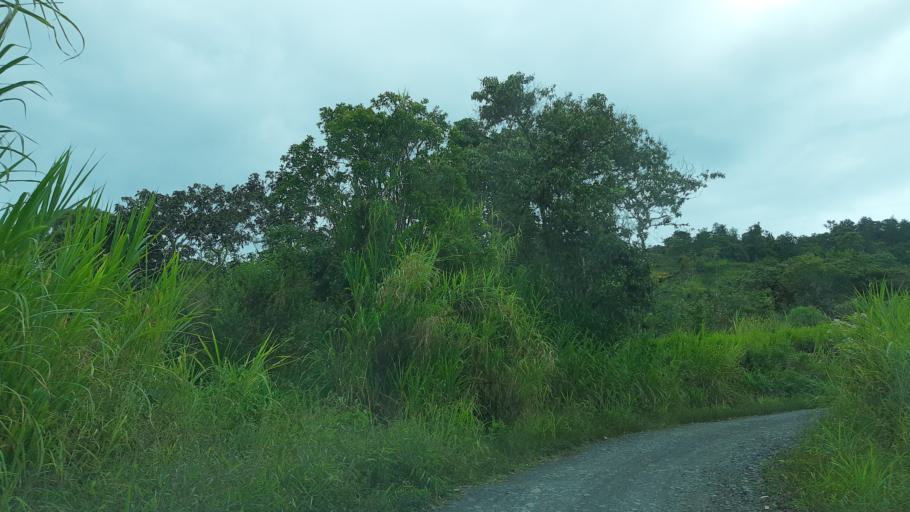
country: CO
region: Boyaca
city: Garagoa
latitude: 5.0183
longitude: -73.3314
